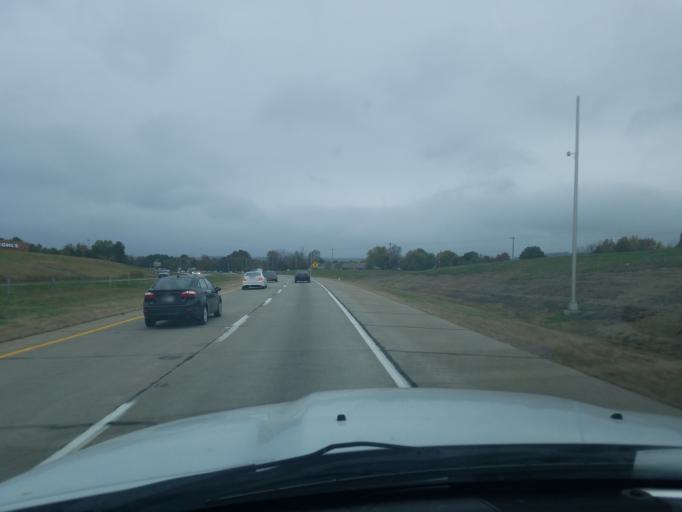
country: US
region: Indiana
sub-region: Clark County
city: Clarksville
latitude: 38.3436
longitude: -85.7991
